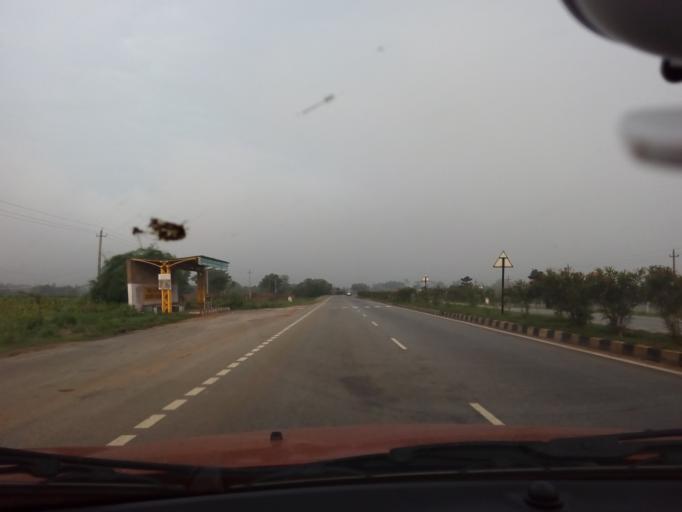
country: IN
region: Karnataka
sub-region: Tumkur
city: Kunigal
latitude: 13.0412
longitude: 77.1250
